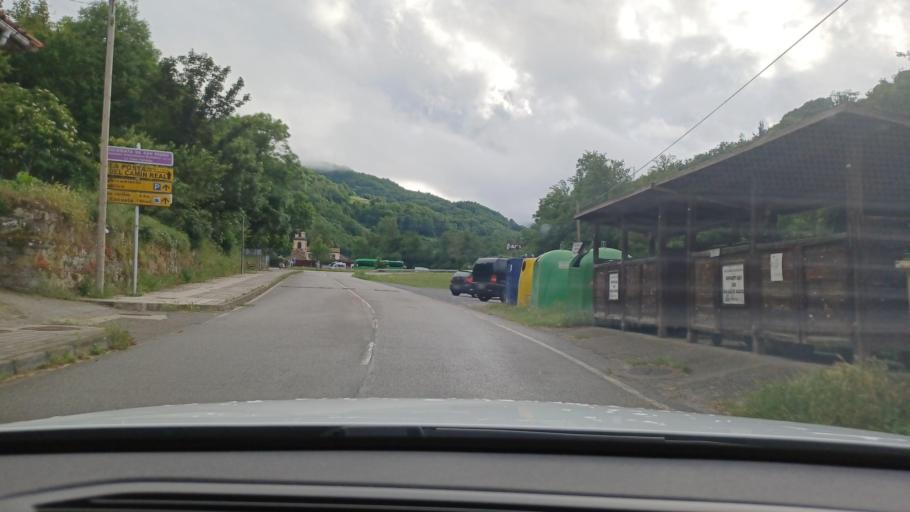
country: ES
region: Asturias
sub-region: Province of Asturias
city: La Plaza
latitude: 43.1605
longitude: -6.0990
